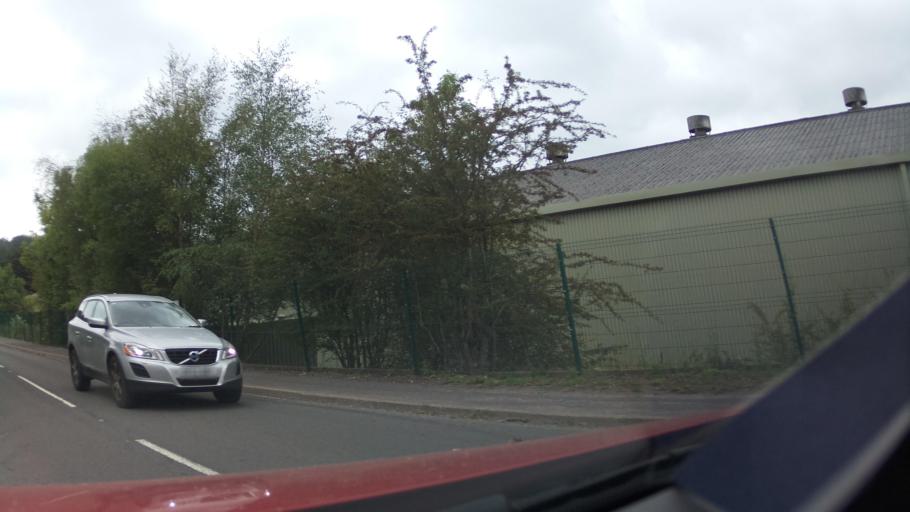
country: GB
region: England
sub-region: Staffordshire
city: Cheadle
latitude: 53.0230
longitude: -1.9635
